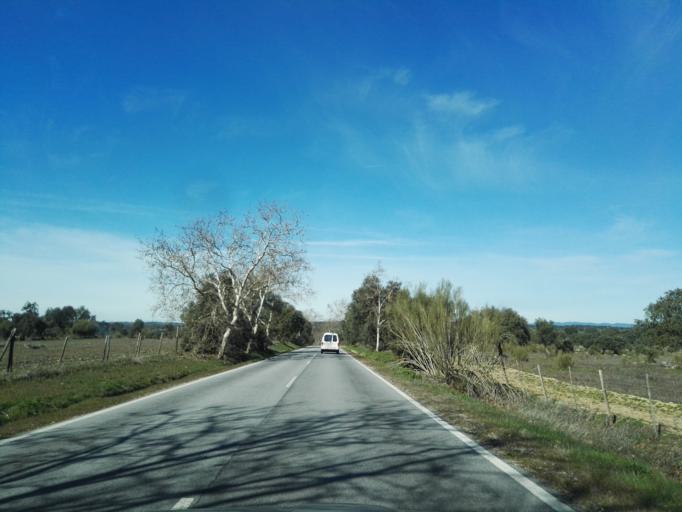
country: PT
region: Portalegre
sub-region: Arronches
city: Arronches
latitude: 39.0475
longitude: -7.2642
